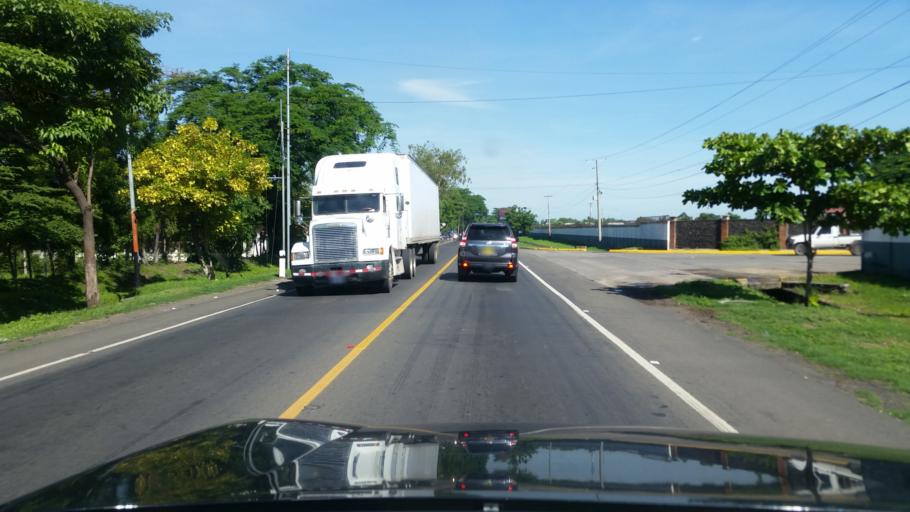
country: NI
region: Chinandega
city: Chinandega
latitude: 12.6176
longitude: -87.1073
